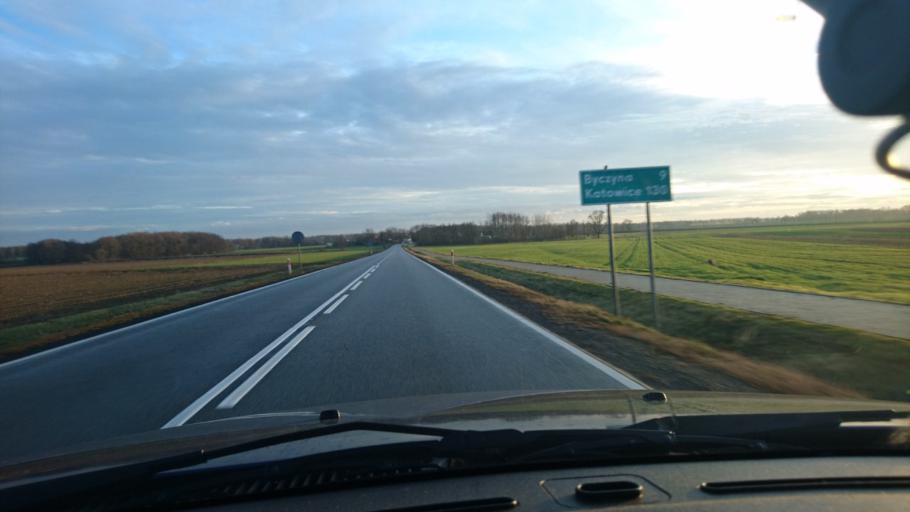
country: PL
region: Greater Poland Voivodeship
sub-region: Powiat kepinski
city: Opatow
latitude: 51.1749
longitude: 18.1446
